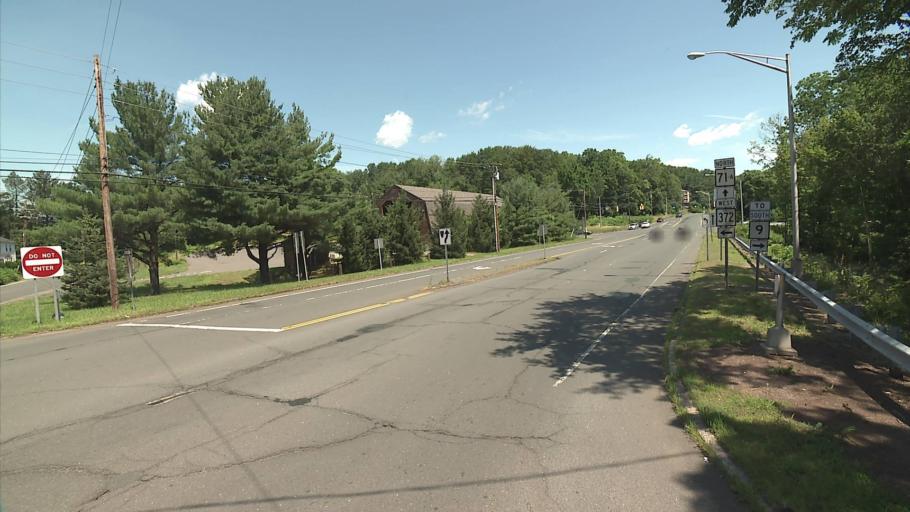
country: US
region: Connecticut
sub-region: Hartford County
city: New Britain
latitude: 41.6458
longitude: -72.7892
